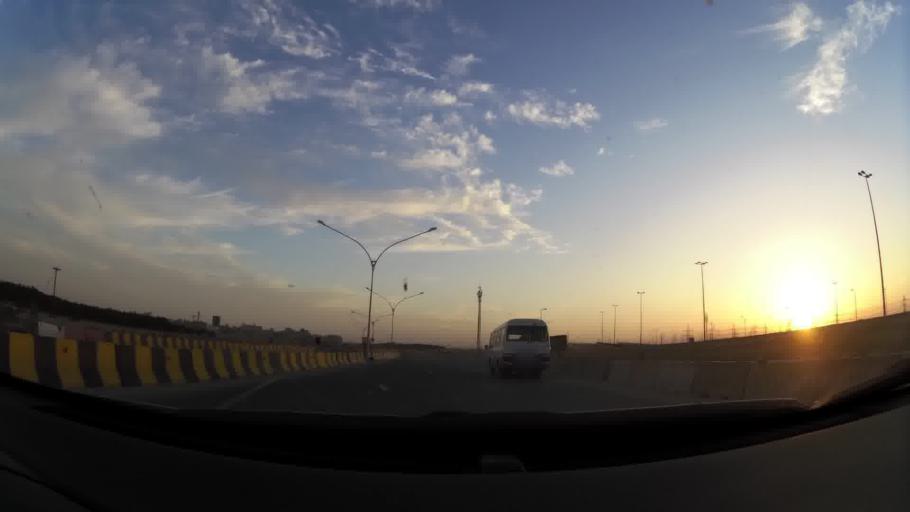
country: KW
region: Al Asimah
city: Ar Rabiyah
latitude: 29.3398
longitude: 47.8010
